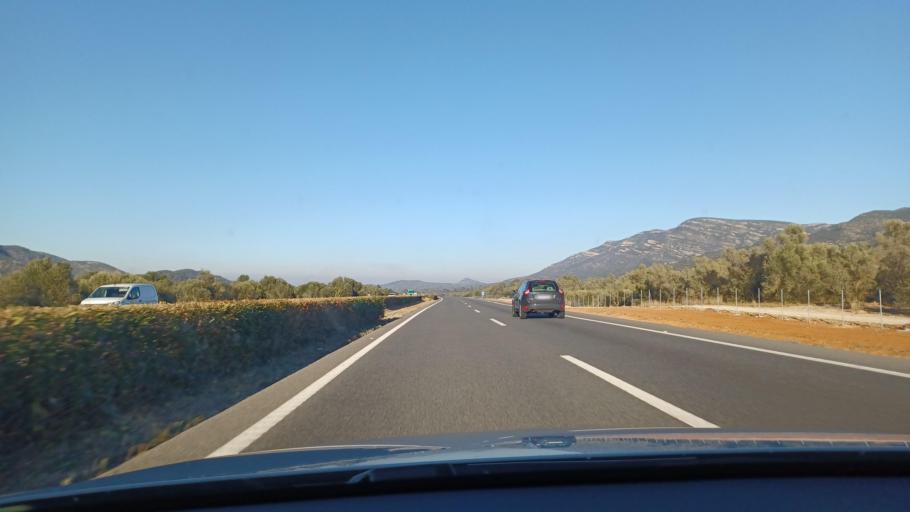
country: ES
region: Catalonia
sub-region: Provincia de Tarragona
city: Ulldecona
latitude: 40.6188
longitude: 0.4837
